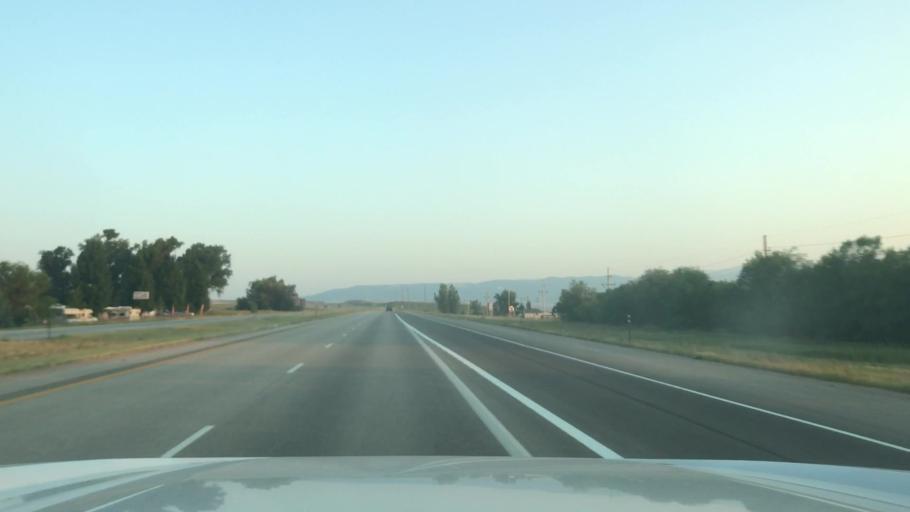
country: US
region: Wyoming
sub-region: Sheridan County
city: Sheridan
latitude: 44.7689
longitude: -106.9370
